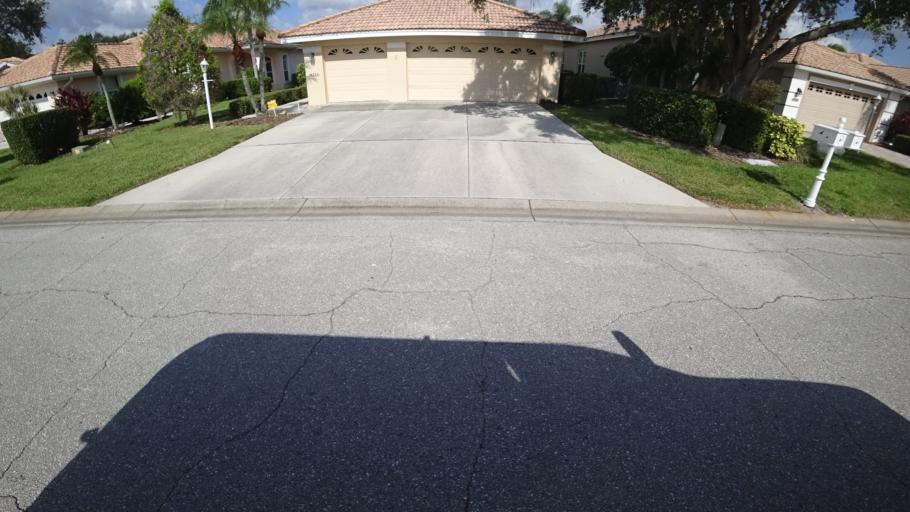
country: US
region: Florida
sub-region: Sarasota County
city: The Meadows
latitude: 27.4210
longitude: -82.4354
